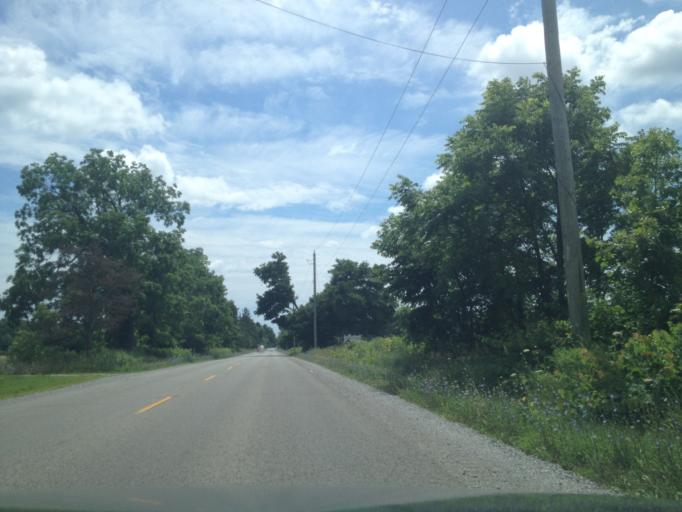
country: CA
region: Ontario
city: Norfolk County
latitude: 42.8114
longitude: -80.3214
